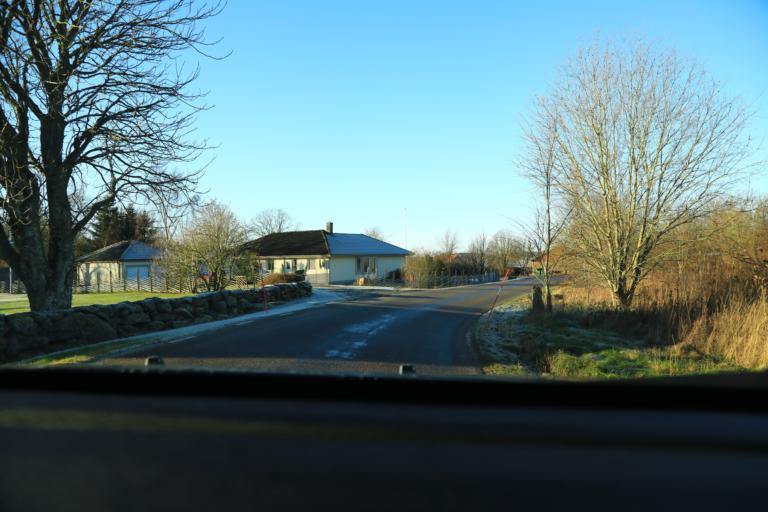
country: SE
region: Halland
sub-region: Varbergs Kommun
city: Varberg
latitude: 57.2055
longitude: 12.2118
